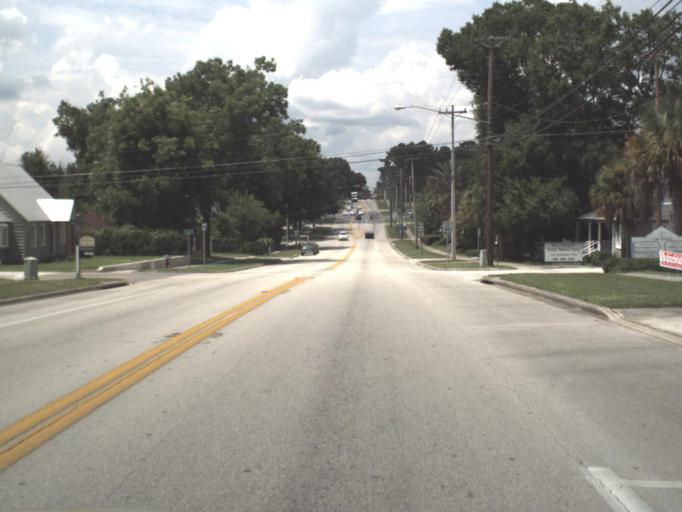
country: US
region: Florida
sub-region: Alachua County
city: Alachua
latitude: 29.7909
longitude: -82.4942
